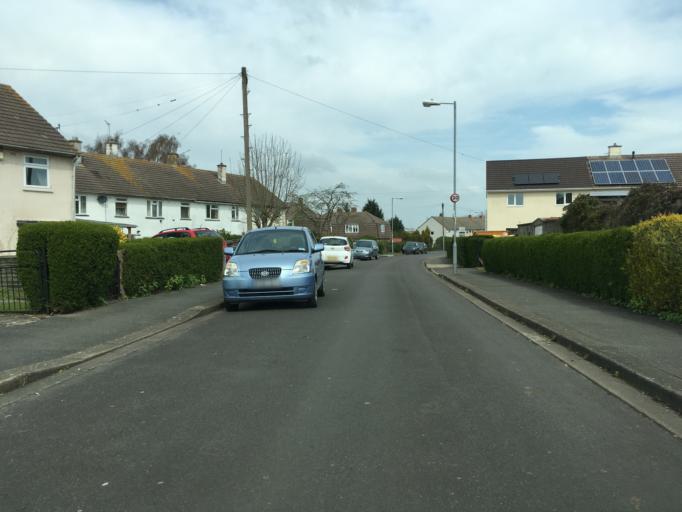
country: GB
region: England
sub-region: South Gloucestershire
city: Almondsbury
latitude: 51.5126
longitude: -2.6020
